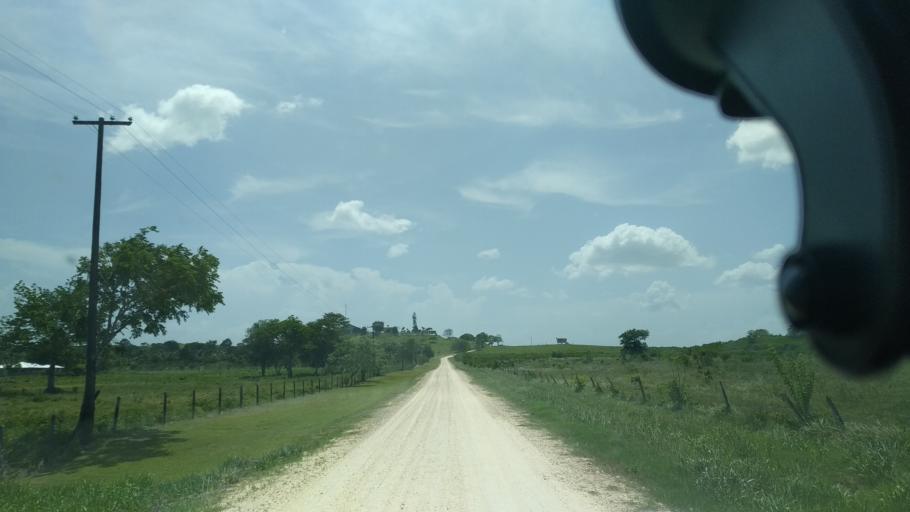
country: BZ
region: Cayo
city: San Ignacio
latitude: 17.3000
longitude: -89.0485
